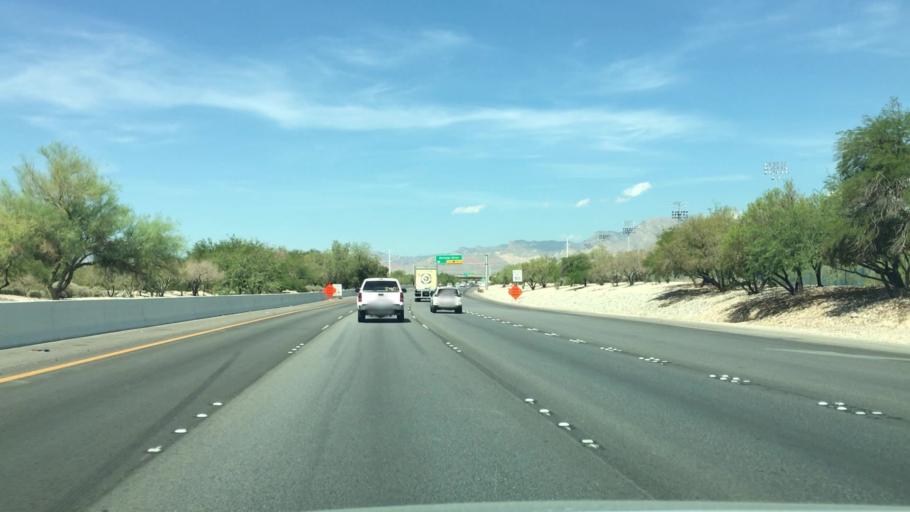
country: US
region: Nevada
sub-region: Clark County
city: Spring Valley
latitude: 36.1784
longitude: -115.2646
